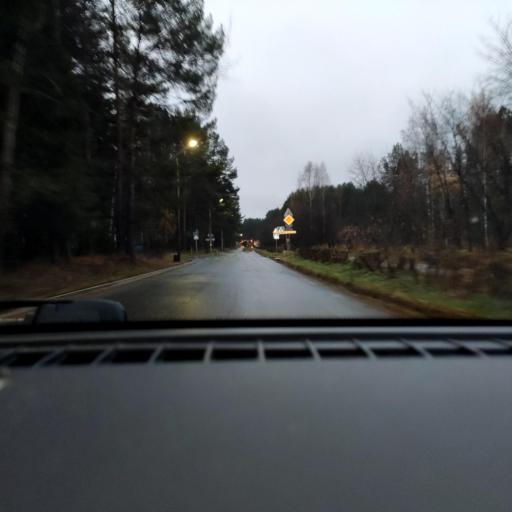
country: RU
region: Perm
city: Perm
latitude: 58.0524
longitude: 56.2142
